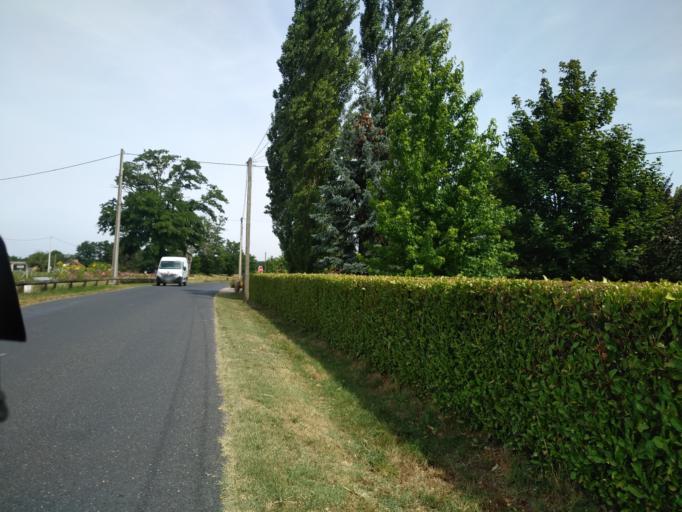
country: FR
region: Auvergne
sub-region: Departement de l'Allier
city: Molinet
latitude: 46.4575
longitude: 3.9645
